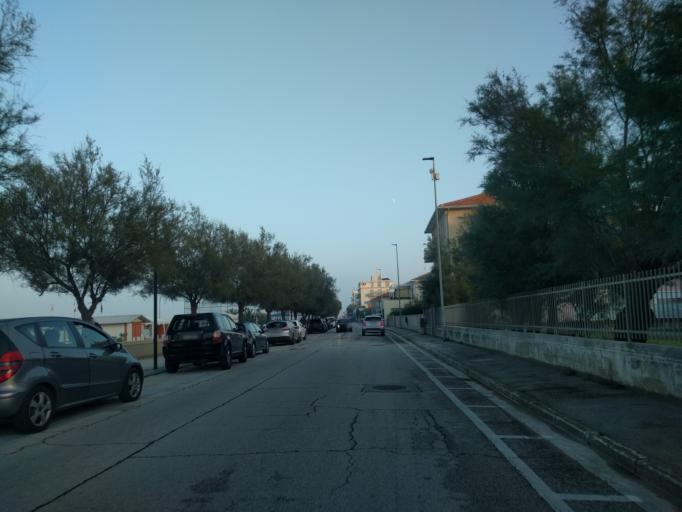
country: IT
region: The Marches
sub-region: Provincia di Ancona
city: Senigallia
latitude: 43.7251
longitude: 13.2094
